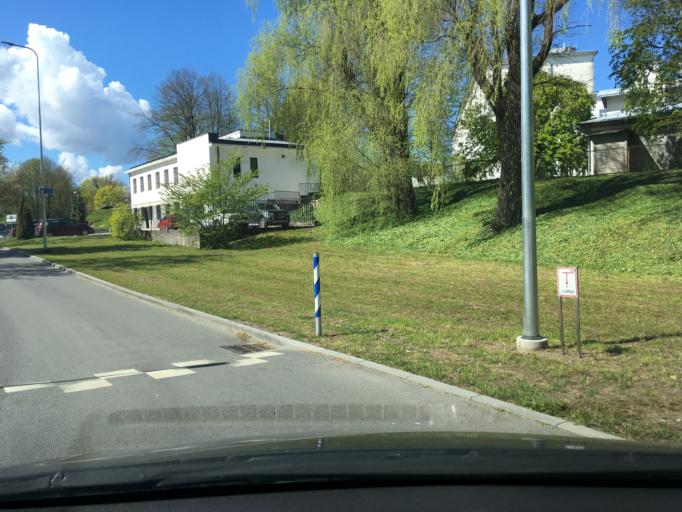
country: EE
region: Harju
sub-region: Tallinna linn
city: Tallinn
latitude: 59.4268
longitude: 24.7583
